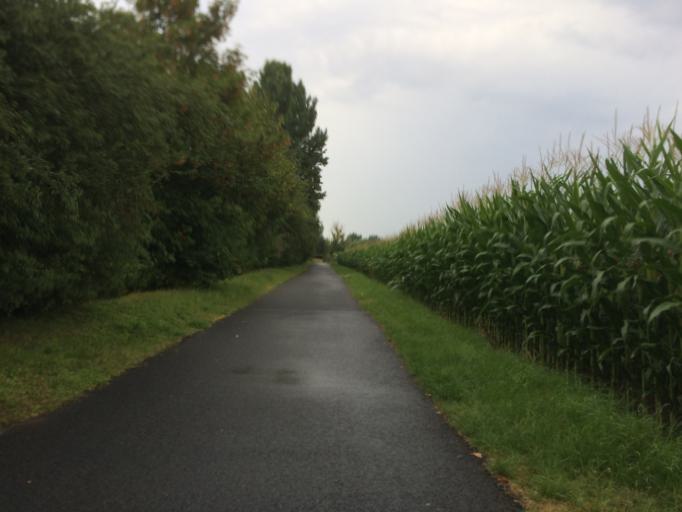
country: FR
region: Picardie
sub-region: Departement de l'Oise
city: Jaux
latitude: 49.3814
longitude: 2.7778
